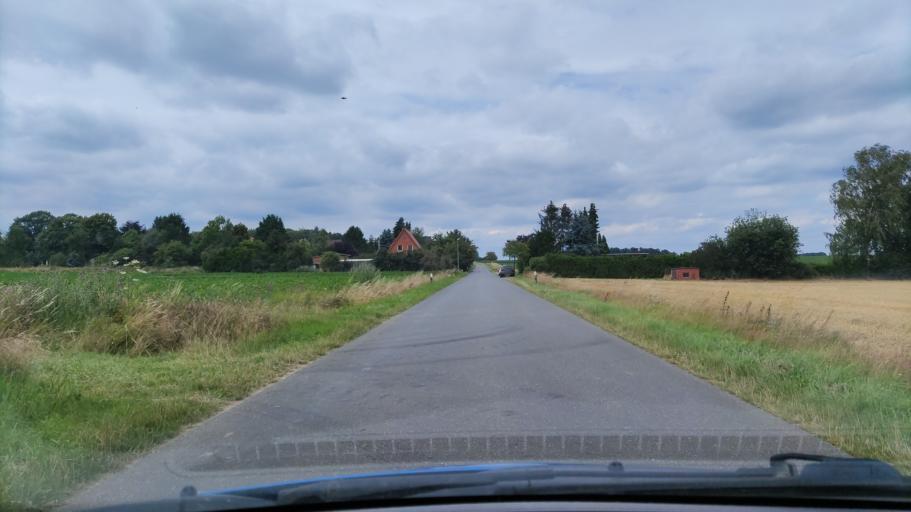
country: DE
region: Lower Saxony
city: Weste
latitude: 53.0633
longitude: 10.6999
